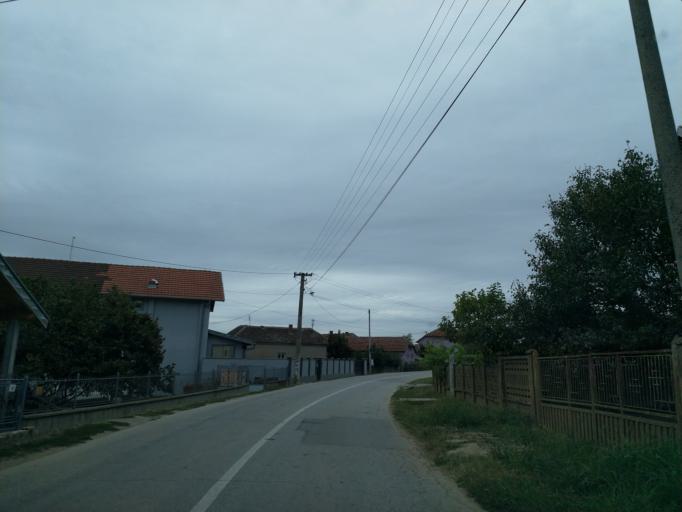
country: RS
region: Central Serbia
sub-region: Pomoravski Okrug
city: Cuprija
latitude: 43.8727
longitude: 21.3220
